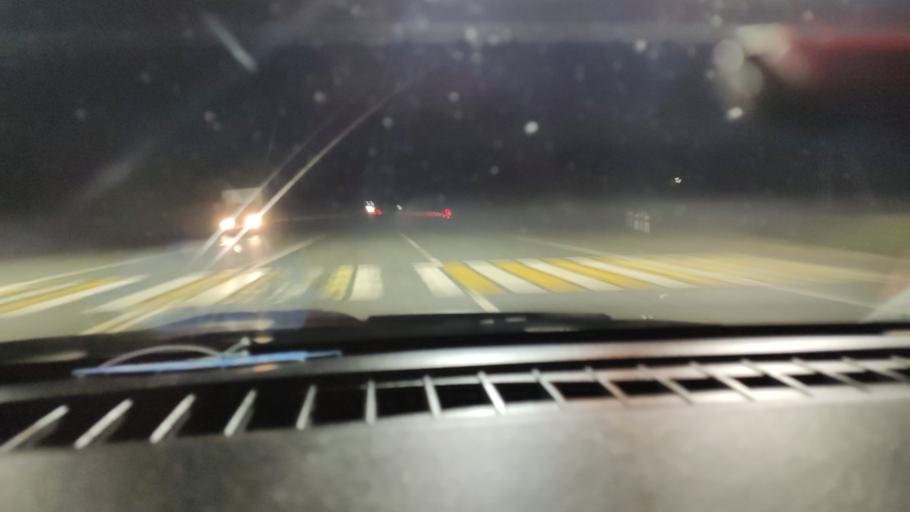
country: RU
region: Udmurtiya
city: Pychas
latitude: 56.4491
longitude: 52.4369
